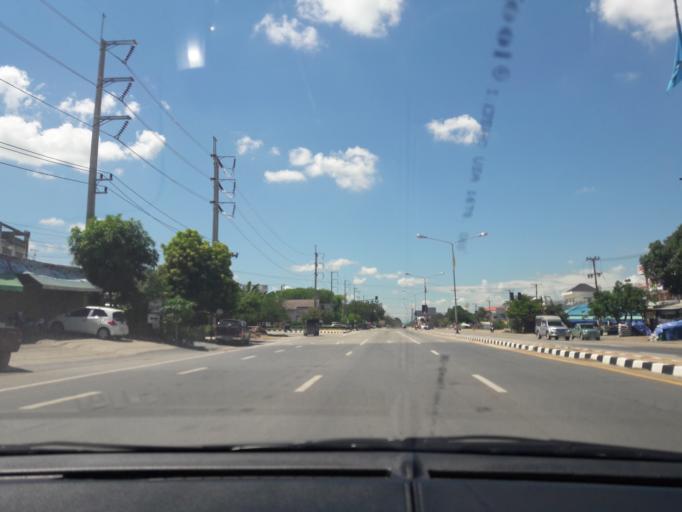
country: TH
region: Kanchanaburi
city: Tha Maka
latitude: 14.0381
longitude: 99.7914
